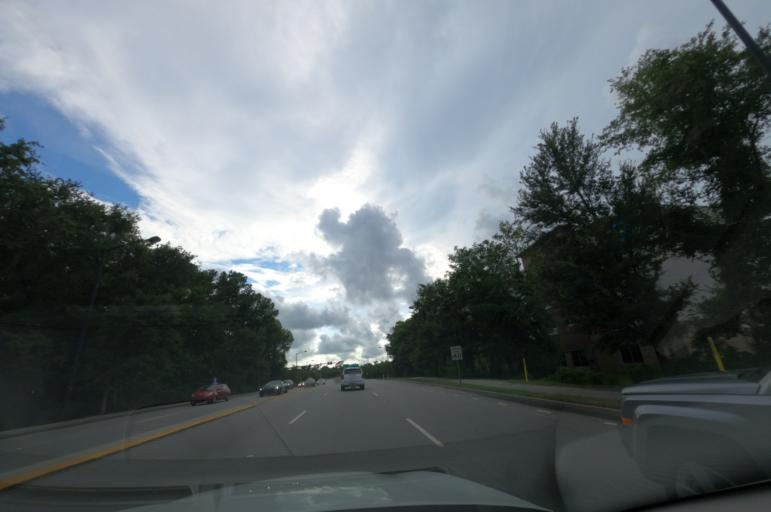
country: US
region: South Carolina
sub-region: Charleston County
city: Mount Pleasant
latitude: 32.8195
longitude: -79.8378
